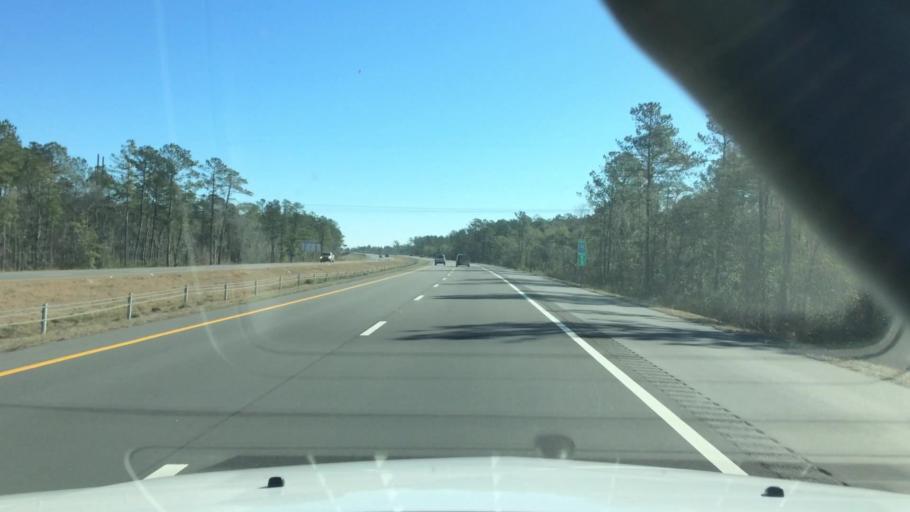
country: US
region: North Carolina
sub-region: Brunswick County
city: Leland
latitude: 34.2735
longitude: -78.0322
